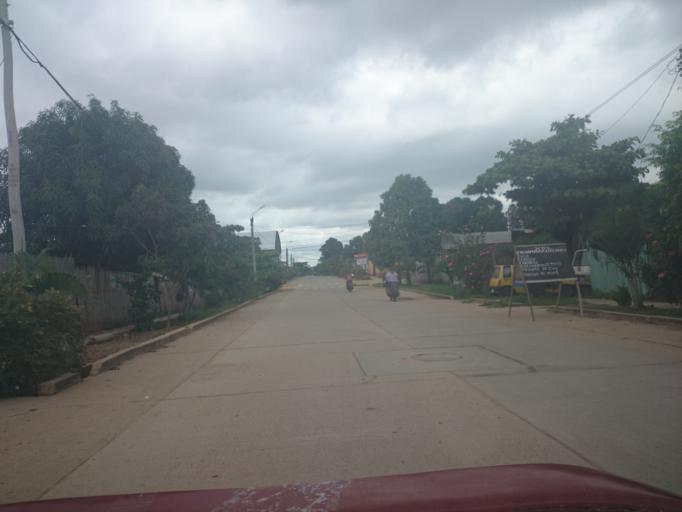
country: PE
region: Ucayali
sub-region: Provincia de Coronel Portillo
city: Puerto Callao
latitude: -8.3627
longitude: -74.5715
